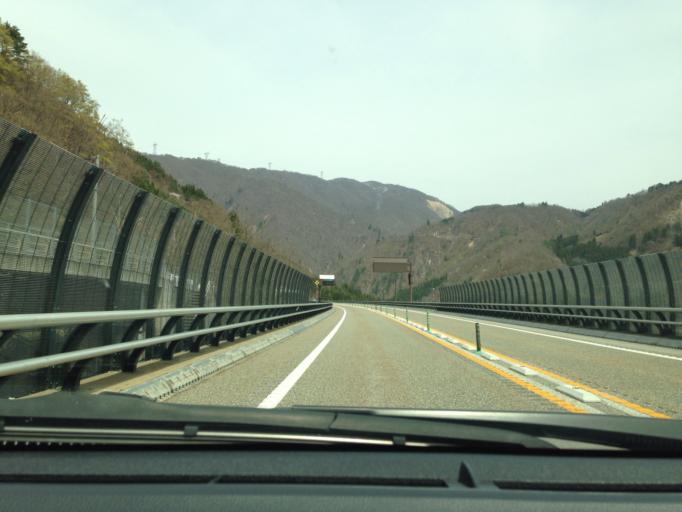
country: JP
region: Toyama
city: Fukumitsu
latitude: 36.2805
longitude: 136.8988
